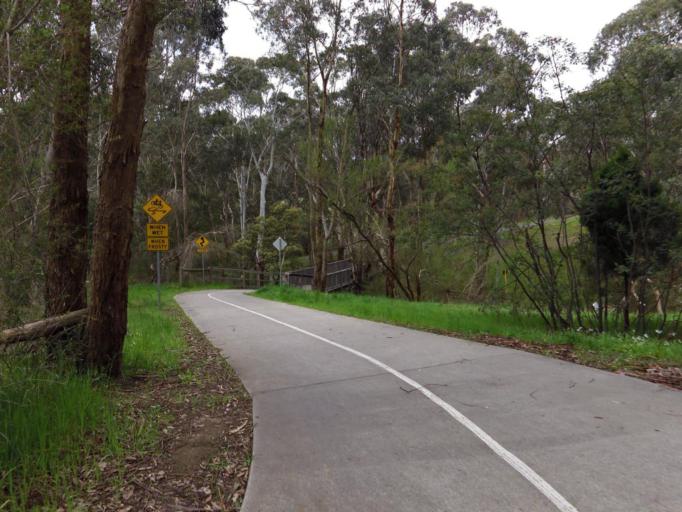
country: AU
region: Victoria
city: Mitcham
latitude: -37.8041
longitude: 145.2030
